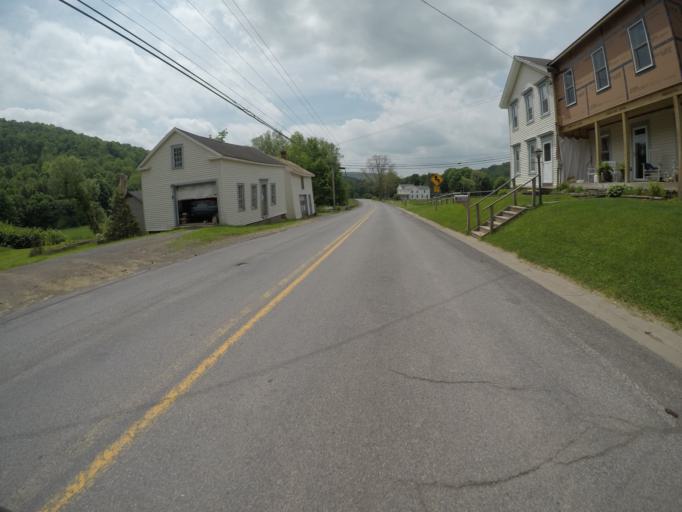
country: US
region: New York
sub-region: Delaware County
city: Delhi
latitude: 42.2603
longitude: -74.7903
